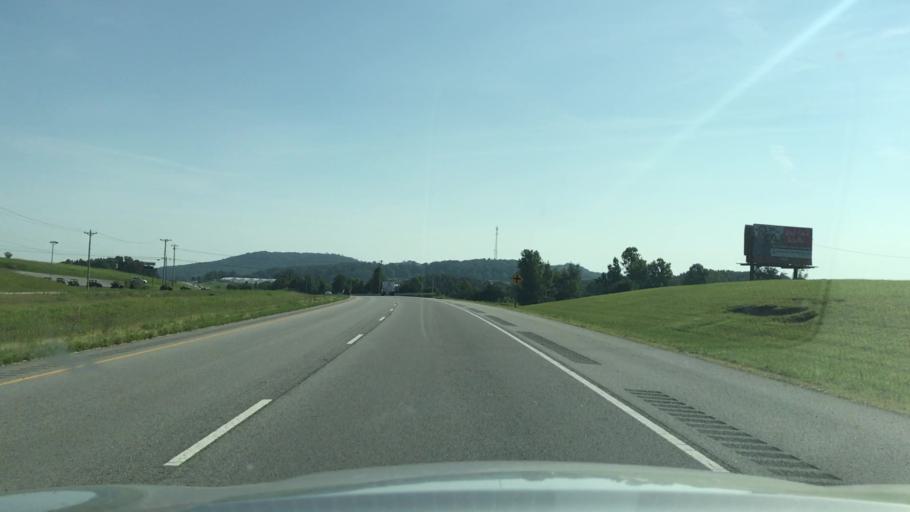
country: US
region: Tennessee
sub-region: Putnam County
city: Algood
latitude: 36.2819
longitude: -85.3771
